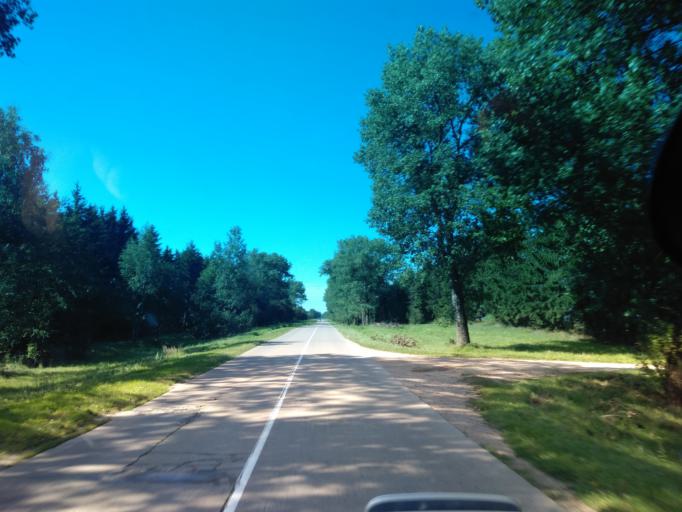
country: BY
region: Minsk
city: Stan'kava
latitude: 53.6545
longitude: 27.3143
